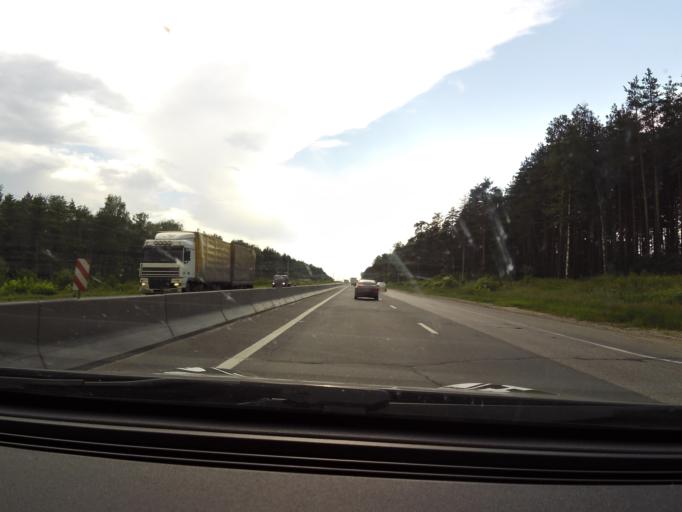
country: RU
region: Nizjnij Novgorod
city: Novosmolinskiy
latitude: 56.2799
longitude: 43.0520
